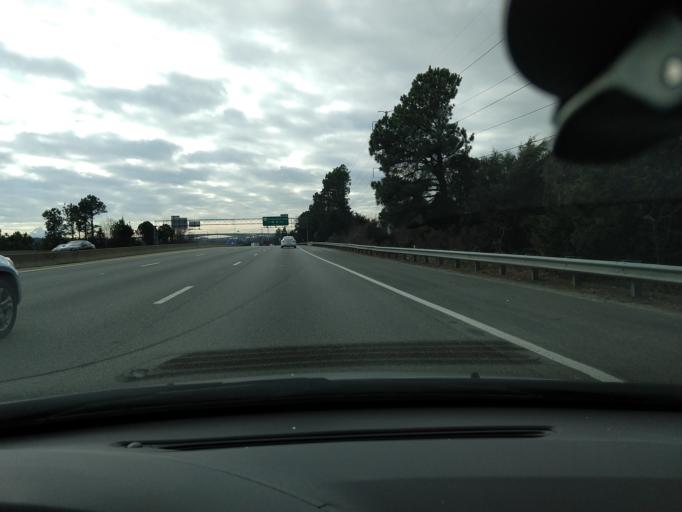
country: US
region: Virginia
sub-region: Chesterfield County
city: Bensley
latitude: 37.4584
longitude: -77.4256
